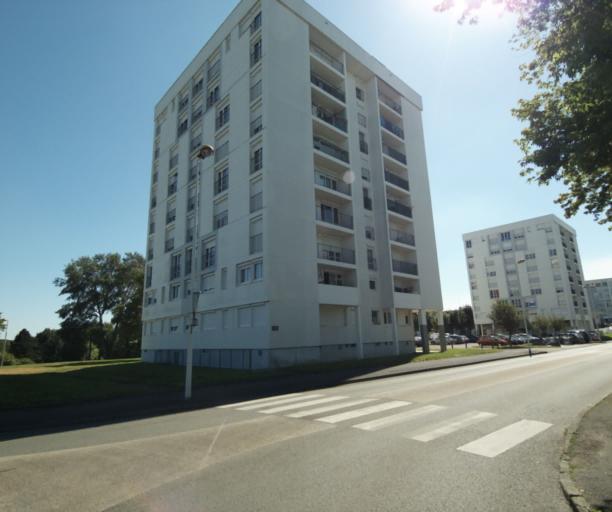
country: FR
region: Pays de la Loire
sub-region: Departement de la Mayenne
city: Laval
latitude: 48.0585
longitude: -0.7451
